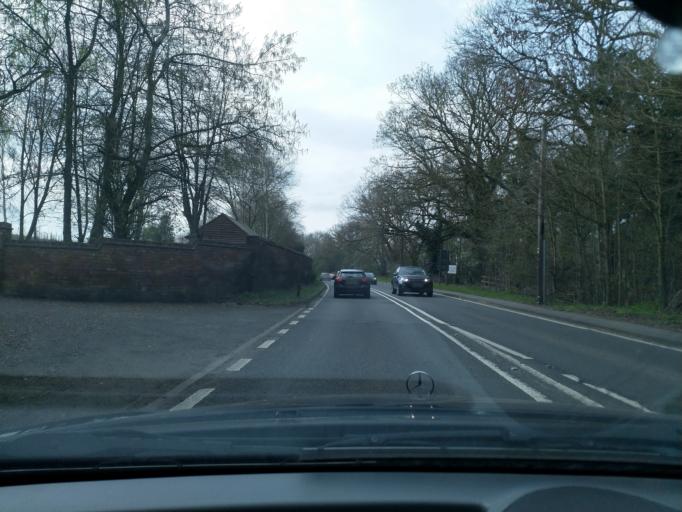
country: GB
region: England
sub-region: Warwickshire
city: Stratford-upon-Avon
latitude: 52.2141
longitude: -1.6767
